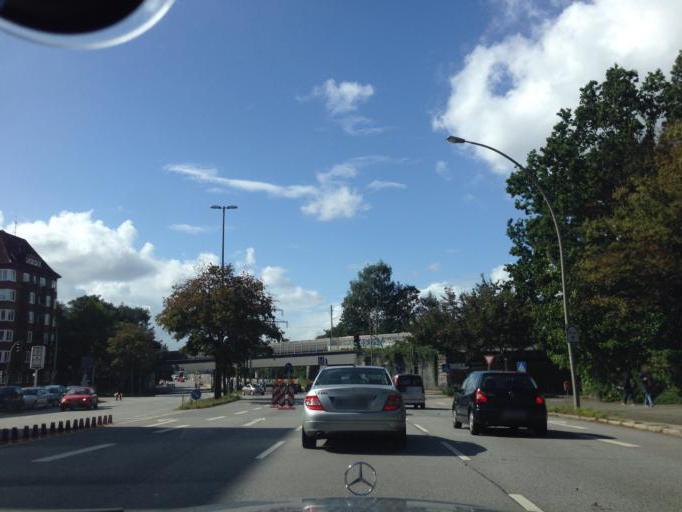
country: DE
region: Hamburg
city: Winterhude
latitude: 53.6019
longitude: 9.9983
